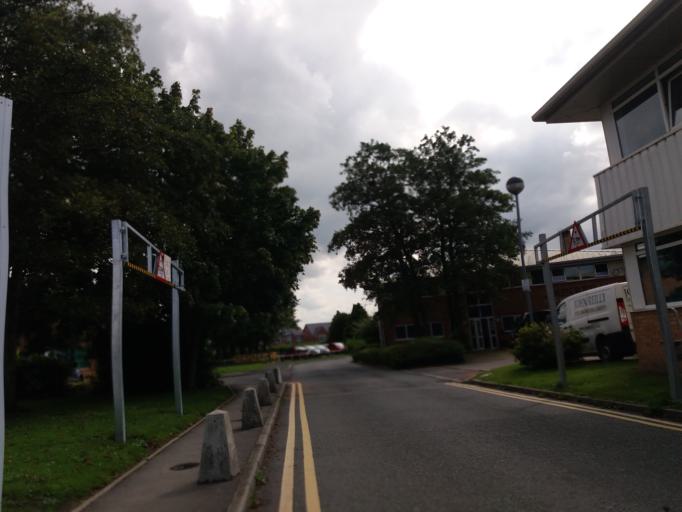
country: GB
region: England
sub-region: Lancashire
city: Euxton
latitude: 53.6730
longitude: -2.6674
